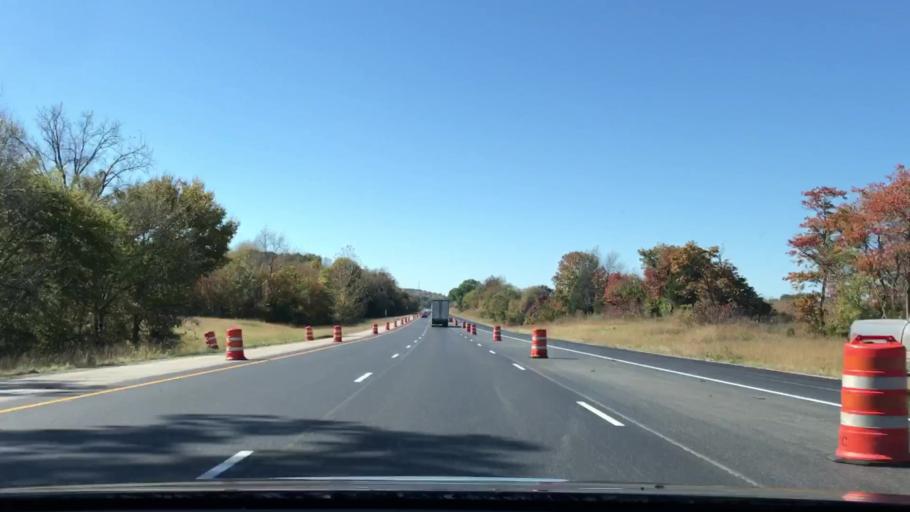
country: US
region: Kentucky
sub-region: Edmonson County
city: Brownsville
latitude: 37.0530
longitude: -86.1384
